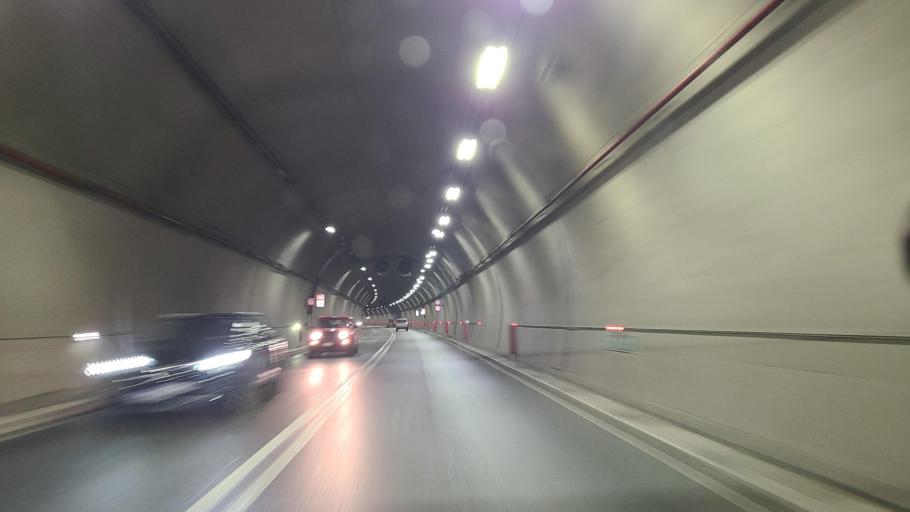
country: IT
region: Tuscany
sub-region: Province of Florence
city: Tavarnuzze
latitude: 43.7369
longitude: 11.2135
